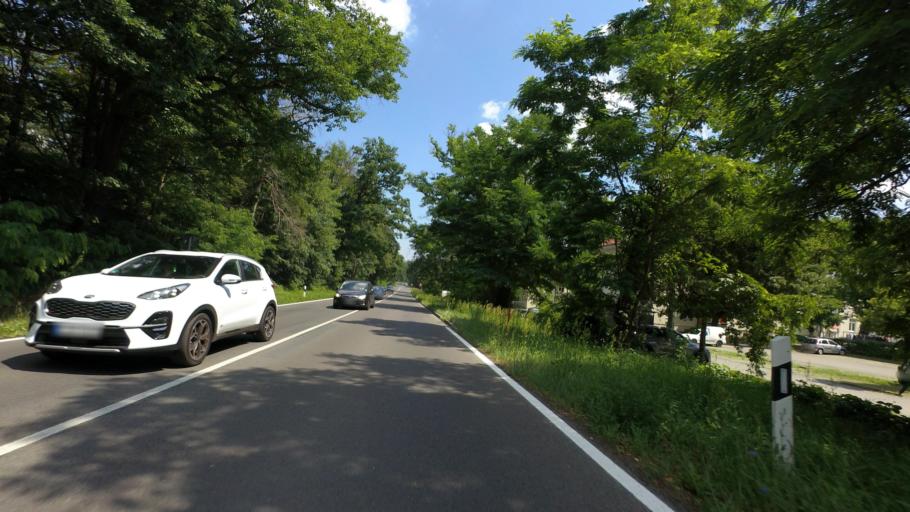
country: DE
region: Brandenburg
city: Bad Freienwalde
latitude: 52.7730
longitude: 14.0063
